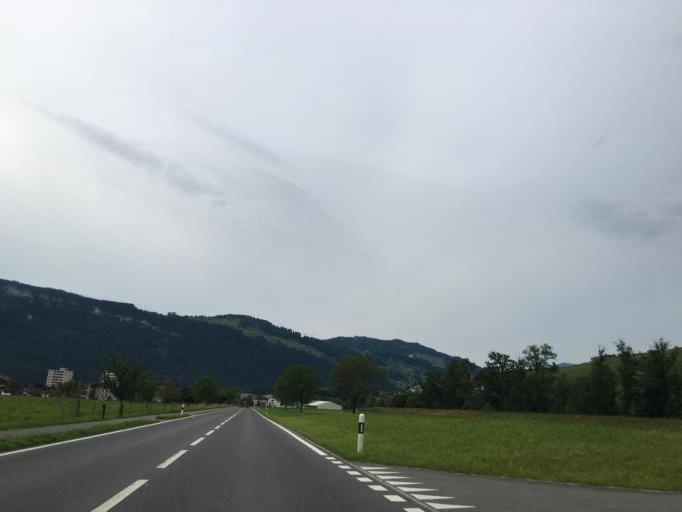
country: CH
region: Nidwalden
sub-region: Nidwalden
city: Stans
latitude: 46.9502
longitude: 8.3877
